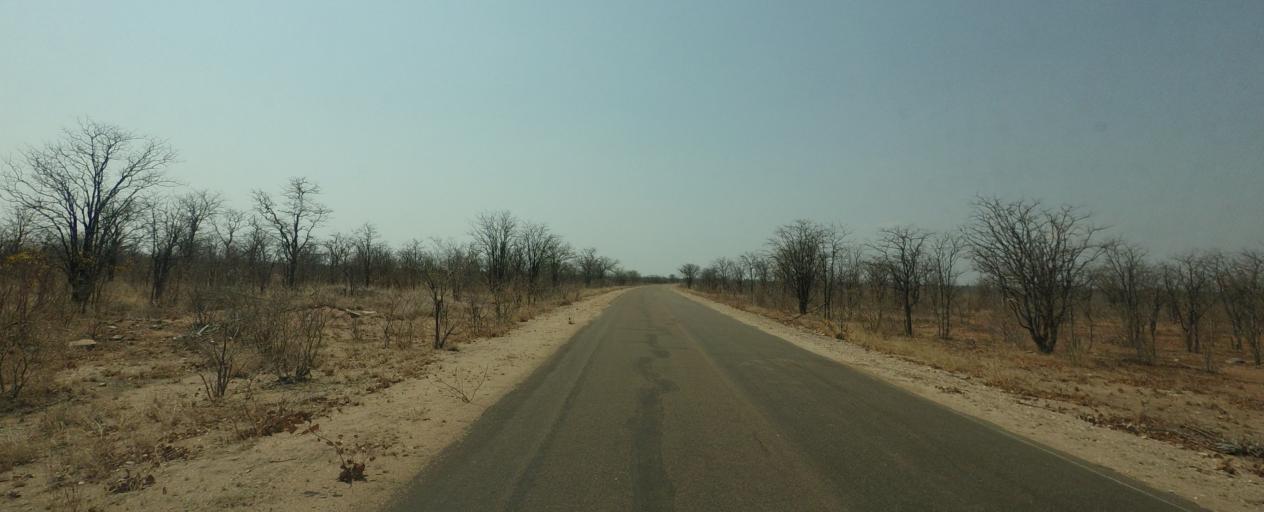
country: ZA
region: Limpopo
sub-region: Mopani District Municipality
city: Giyani
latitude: -23.3522
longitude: 31.3188
